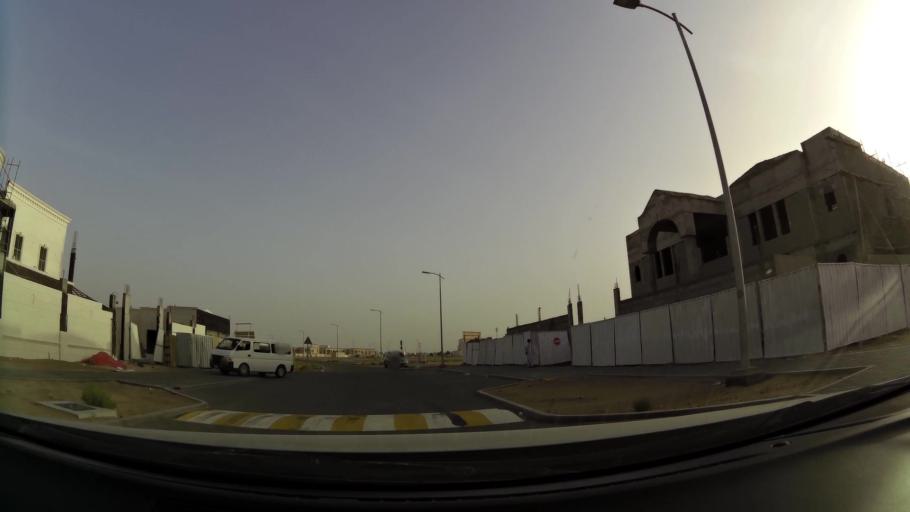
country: AE
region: Abu Dhabi
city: Al Ain
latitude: 24.1069
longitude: 55.7156
